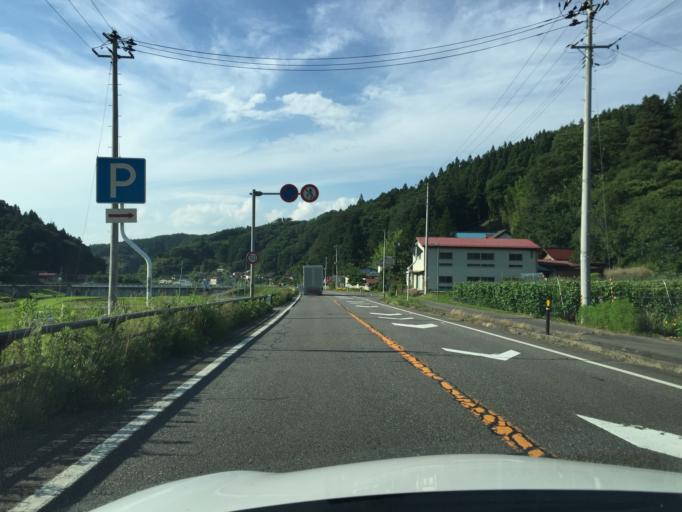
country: JP
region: Fukushima
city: Sukagawa
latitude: 37.2995
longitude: 140.4921
